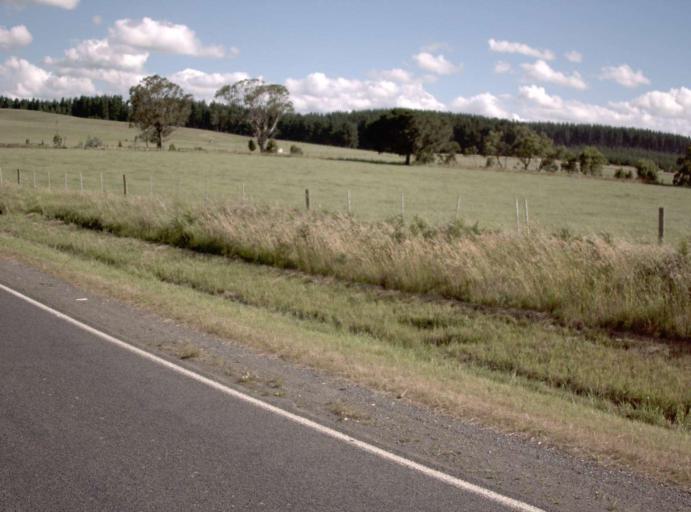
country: AU
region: Victoria
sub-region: Latrobe
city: Morwell
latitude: -38.1709
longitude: 146.4152
